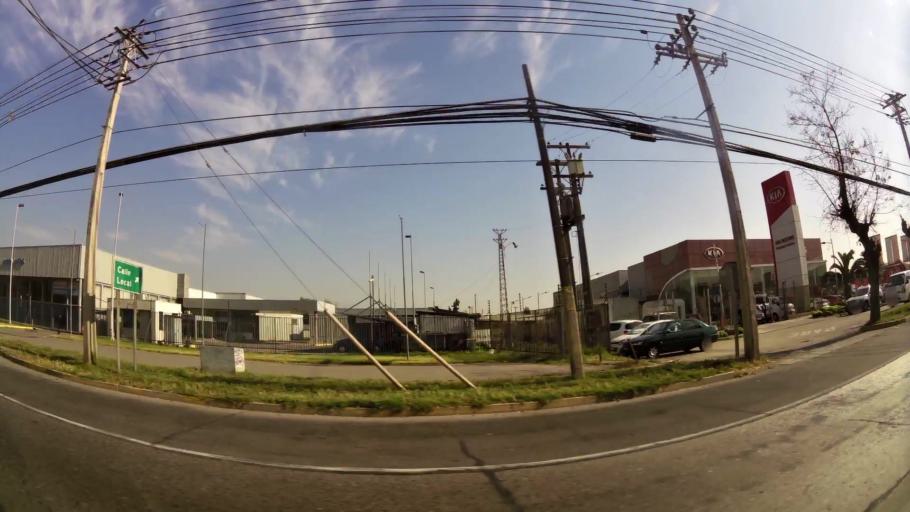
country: CL
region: Santiago Metropolitan
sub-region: Provincia de Santiago
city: Lo Prado
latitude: -33.5241
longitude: -70.7508
